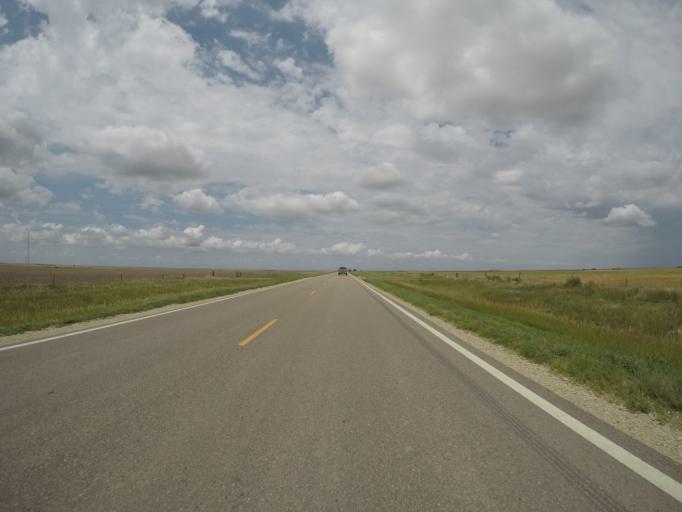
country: US
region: Kansas
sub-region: Rawlins County
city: Atwood
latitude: 39.7274
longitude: -101.0563
